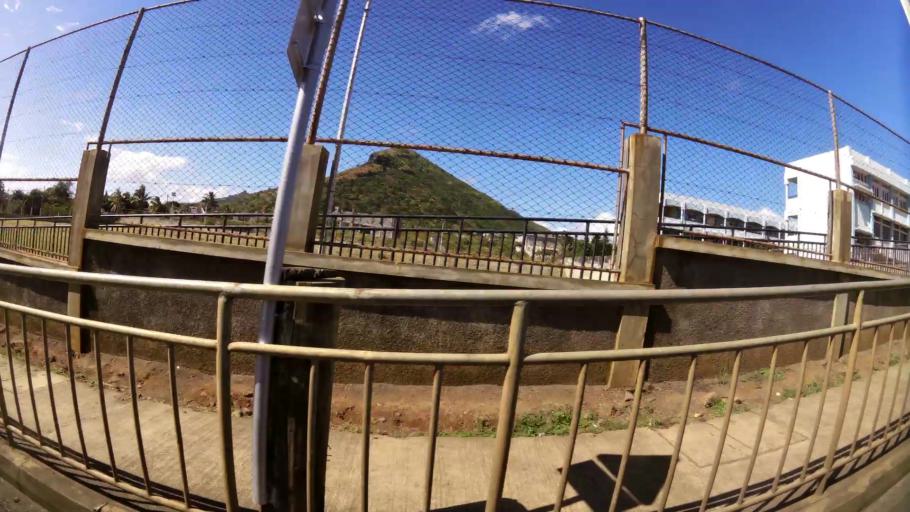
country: MU
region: Black River
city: Cascavelle
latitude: -20.2646
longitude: 57.4166
